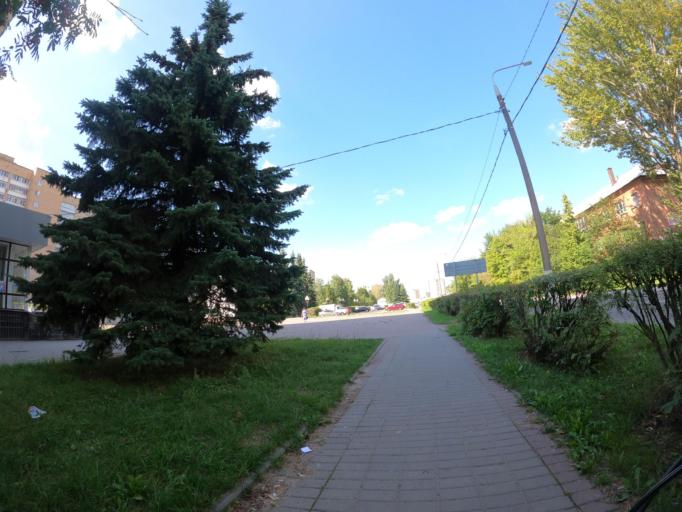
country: RU
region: Moskovskaya
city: Stupino
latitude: 54.8860
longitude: 38.0685
